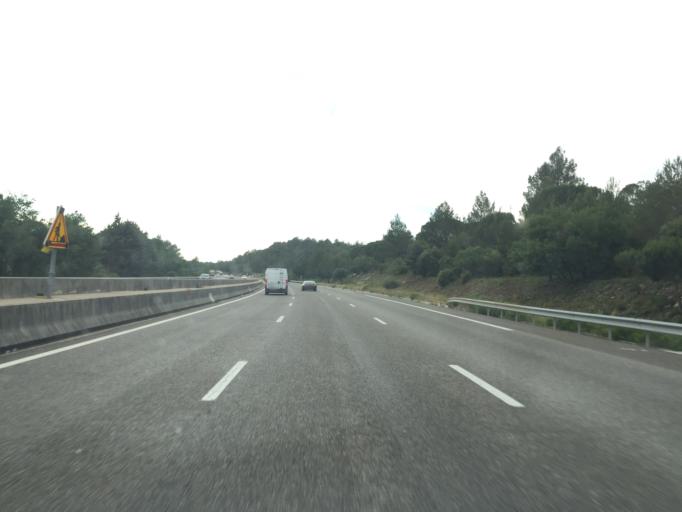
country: FR
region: Provence-Alpes-Cote d'Azur
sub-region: Departement du Var
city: Tourves
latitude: 43.4343
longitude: 5.9334
